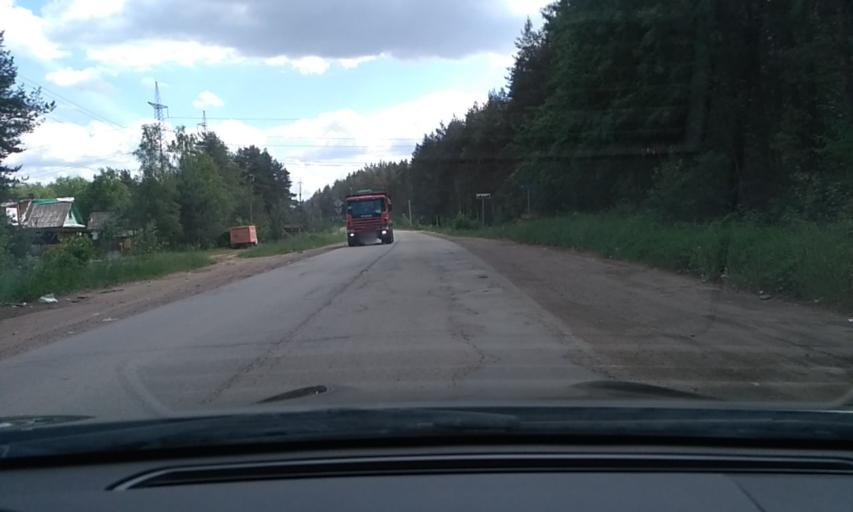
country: RU
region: Leningrad
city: Imeni Sverdlova
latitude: 59.8571
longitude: 30.6727
